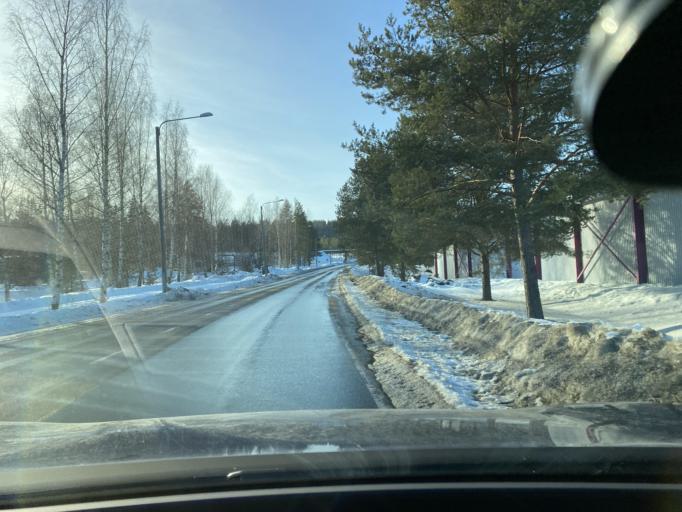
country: FI
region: Central Finland
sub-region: Jyvaeskylae
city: Muurame
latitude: 62.1026
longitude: 25.6476
